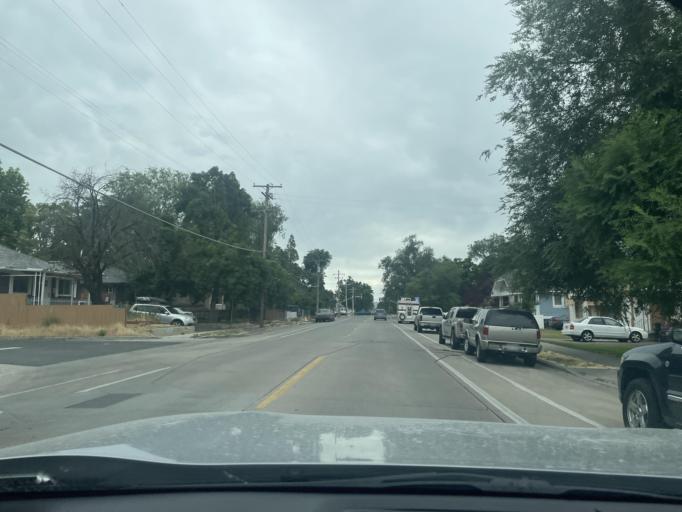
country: US
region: Utah
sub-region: Salt Lake County
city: Millcreek
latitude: 40.7016
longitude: -111.8770
